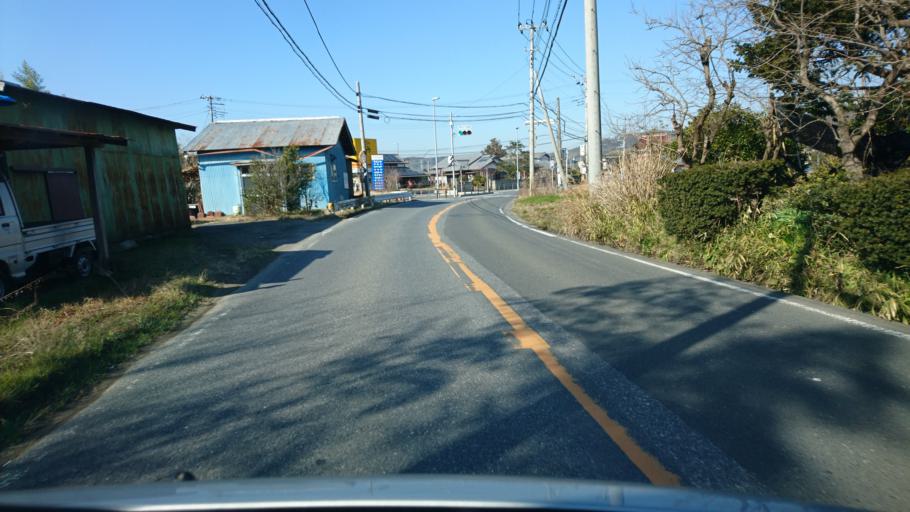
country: JP
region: Chiba
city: Kimitsu
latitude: 35.2996
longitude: 139.9754
